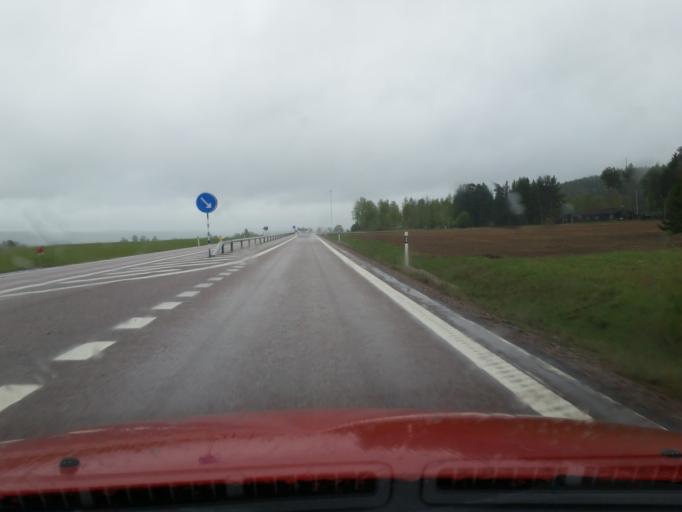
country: SE
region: Dalarna
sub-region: Hedemora Kommun
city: Hedemora
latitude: 60.3052
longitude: 15.9588
